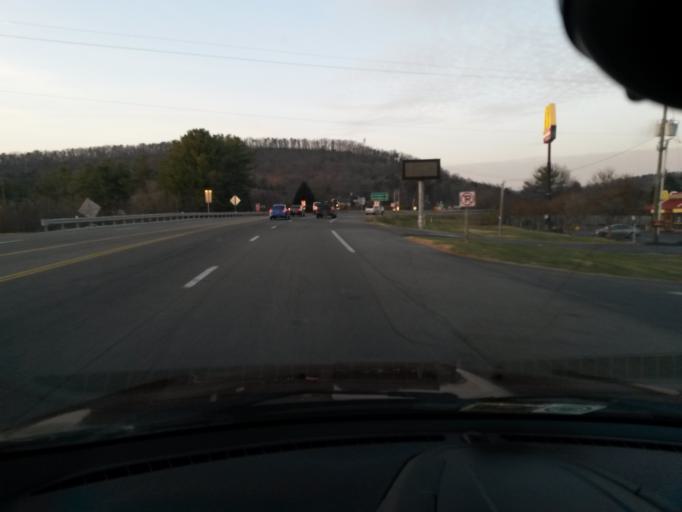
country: US
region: Virginia
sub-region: Roanoke County
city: Hollins
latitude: 37.3593
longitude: -79.9573
